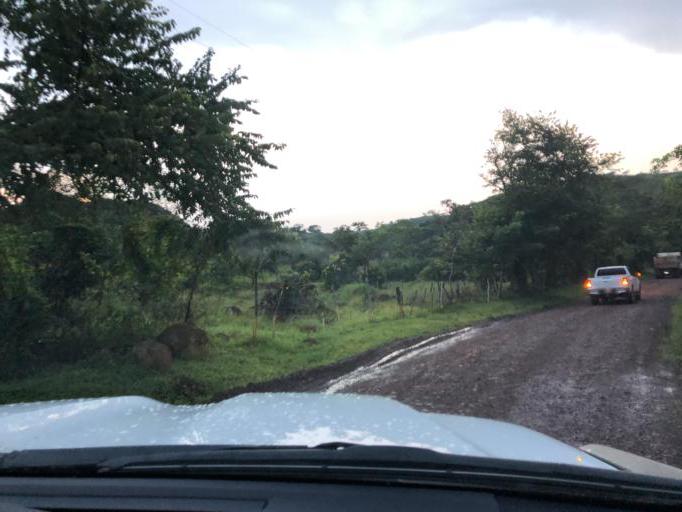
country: NI
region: Chontales
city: La Libertad
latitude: 12.1592
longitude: -85.1784
